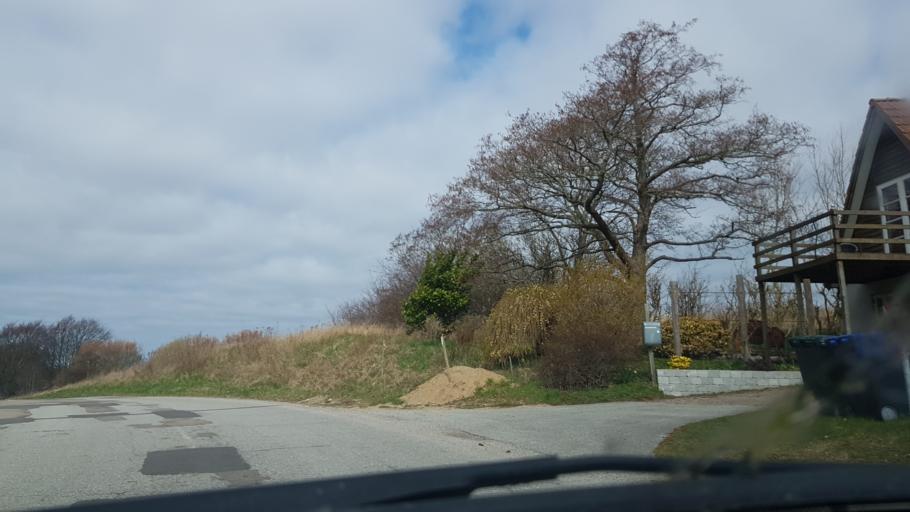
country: DK
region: Zealand
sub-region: Odsherred Kommune
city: Hojby
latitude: 55.9203
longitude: 11.5685
